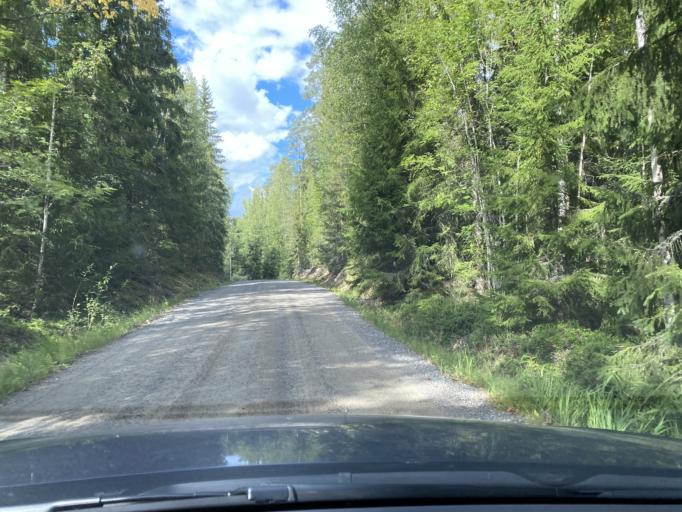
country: FI
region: Haeme
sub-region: Forssa
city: Humppila
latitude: 61.0568
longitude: 23.2650
